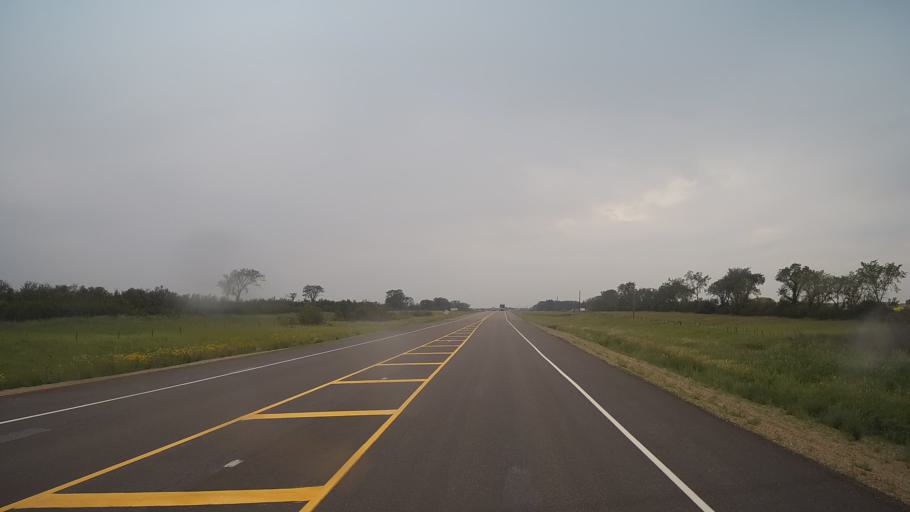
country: CA
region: Saskatchewan
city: Dalmeny
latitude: 52.1293
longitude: -106.8643
